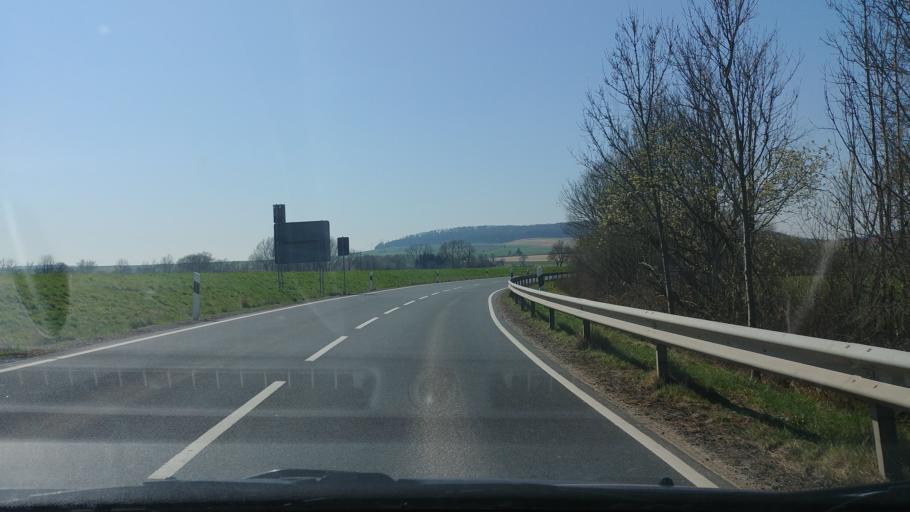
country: DE
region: Lower Saxony
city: Hillerse
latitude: 51.7368
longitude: 9.9472
